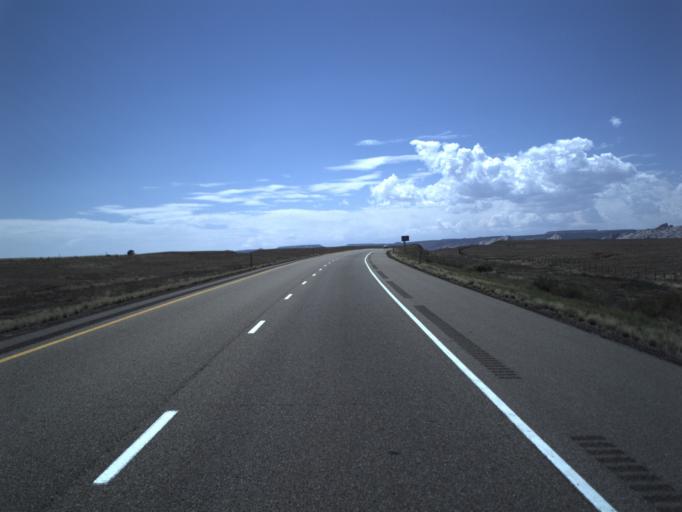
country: US
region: Utah
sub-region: Carbon County
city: East Carbon City
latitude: 38.9440
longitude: -110.3292
